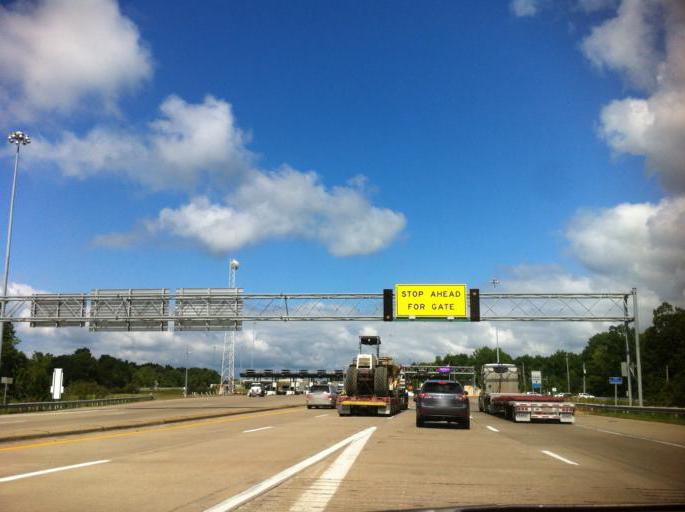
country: US
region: Ohio
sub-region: Trumbull County
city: Lordstown
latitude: 41.1108
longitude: -80.8312
